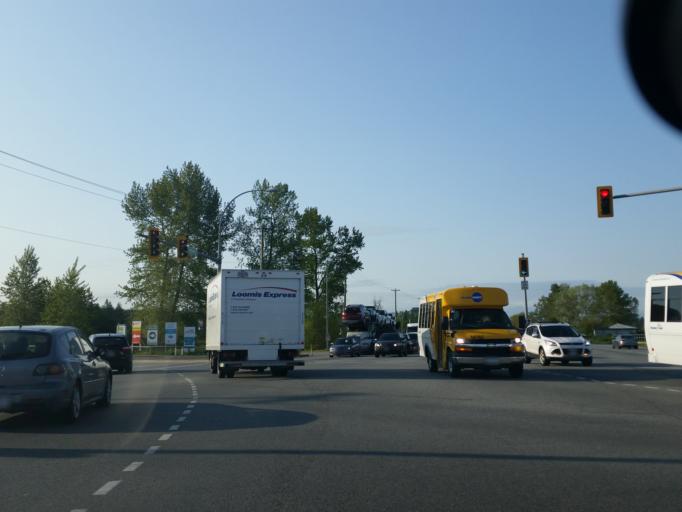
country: CA
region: British Columbia
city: Langley
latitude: 49.1383
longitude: -122.7348
